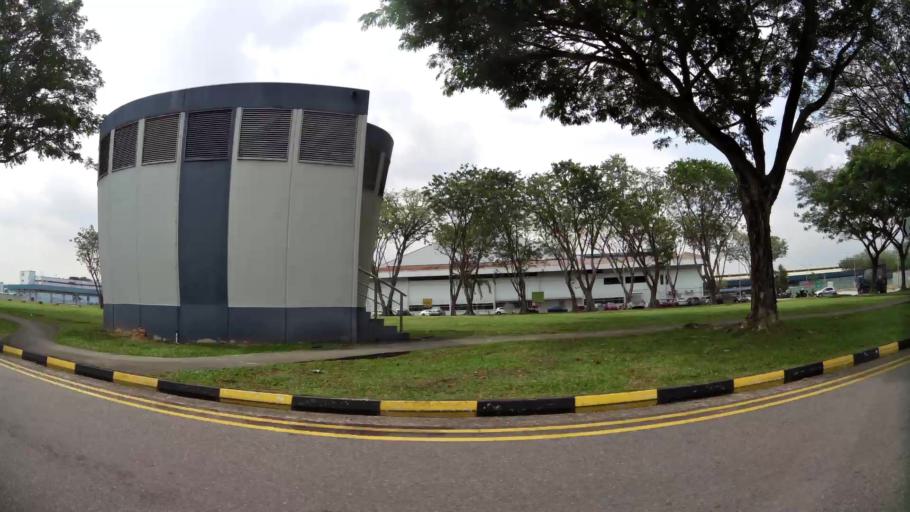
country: SG
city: Singapore
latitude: 1.3495
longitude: 103.8985
